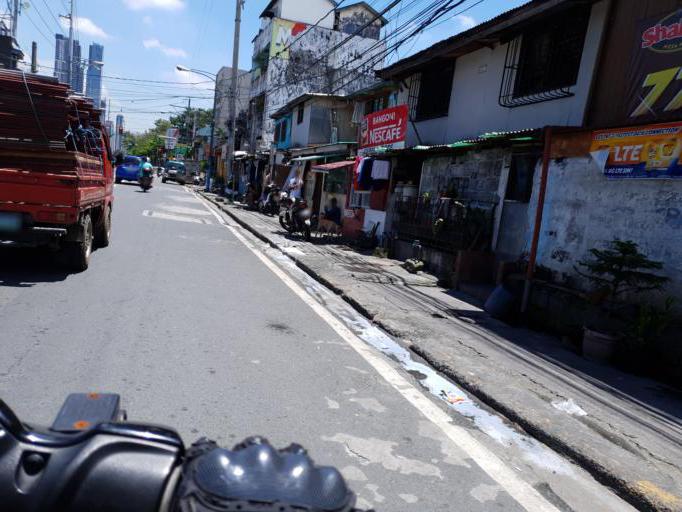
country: PH
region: Metro Manila
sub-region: Makati City
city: Makati City
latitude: 14.5690
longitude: 121.0171
